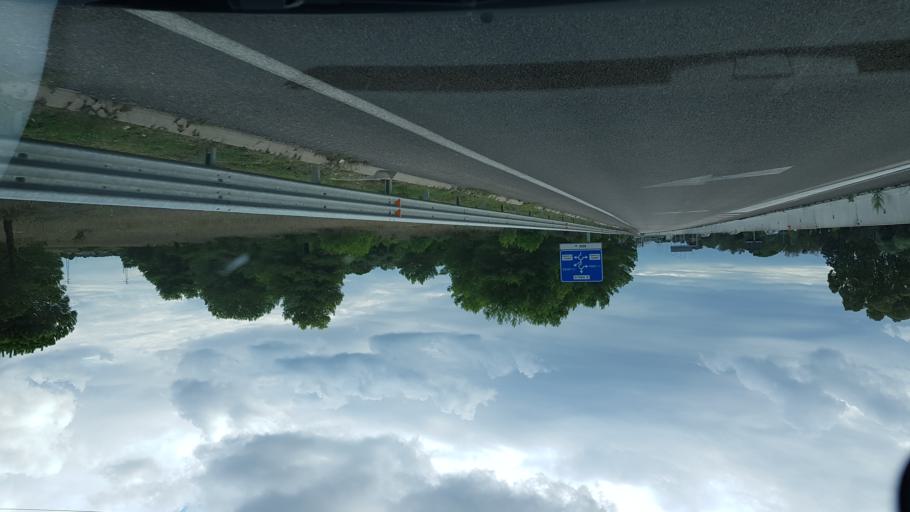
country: IT
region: Apulia
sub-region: Provincia di Lecce
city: Muro Leccese
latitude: 40.1237
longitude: 18.3260
